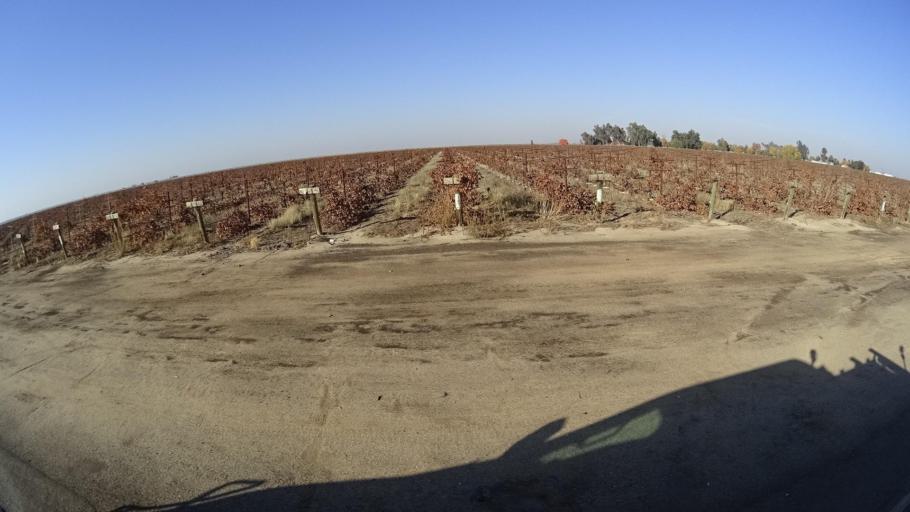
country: US
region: California
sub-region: Kern County
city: Delano
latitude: 35.7418
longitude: -119.1697
